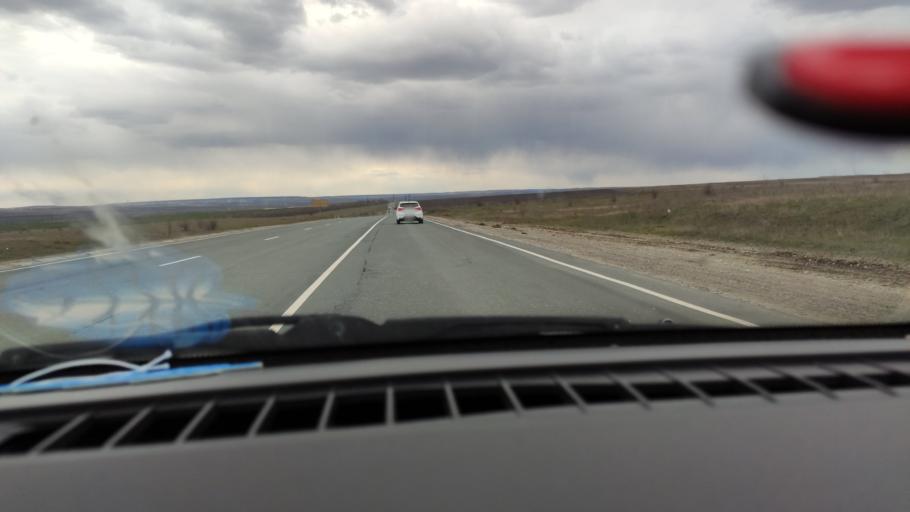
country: RU
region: Saratov
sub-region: Saratovskiy Rayon
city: Saratov
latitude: 51.7583
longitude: 46.0688
